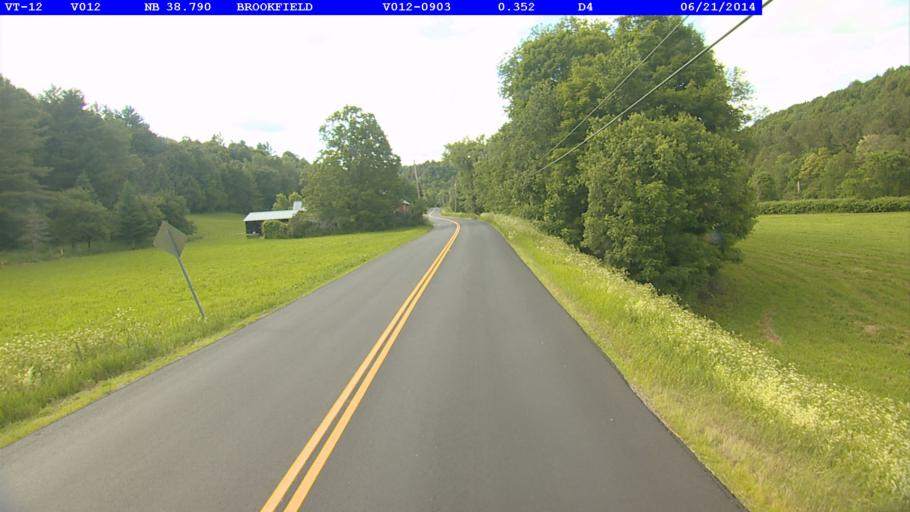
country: US
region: Vermont
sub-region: Orange County
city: Randolph
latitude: 44.0101
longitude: -72.6554
